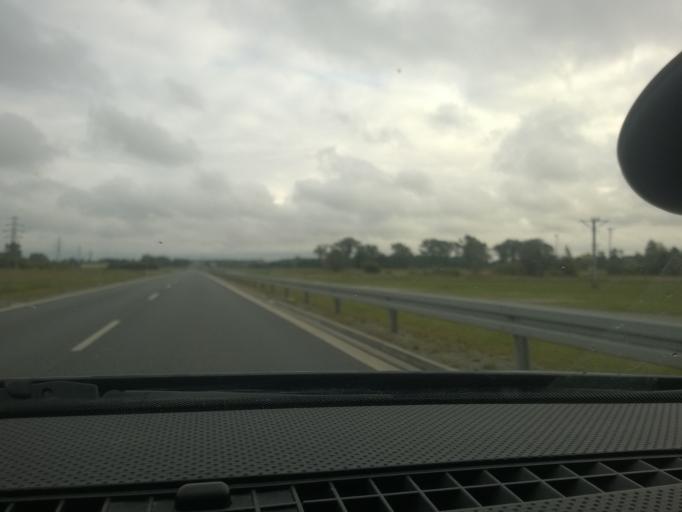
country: PL
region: Lodz Voivodeship
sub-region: Powiat sieradzki
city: Sieradz
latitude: 51.5713
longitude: 18.6966
